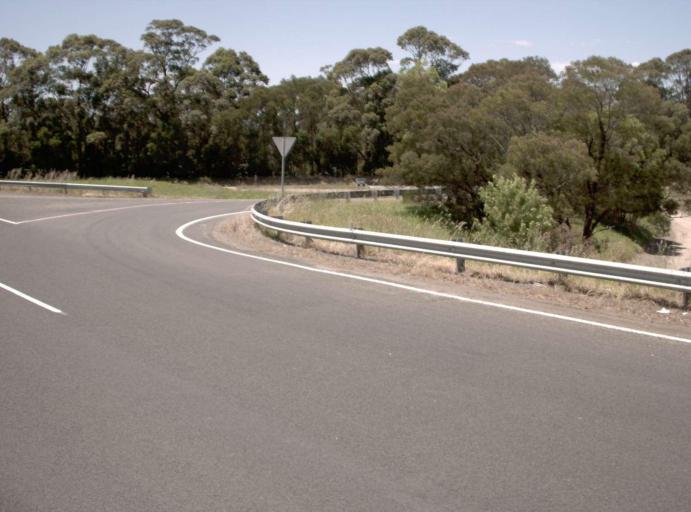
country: AU
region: Victoria
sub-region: East Gippsland
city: Lakes Entrance
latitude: -37.7176
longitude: 148.4528
